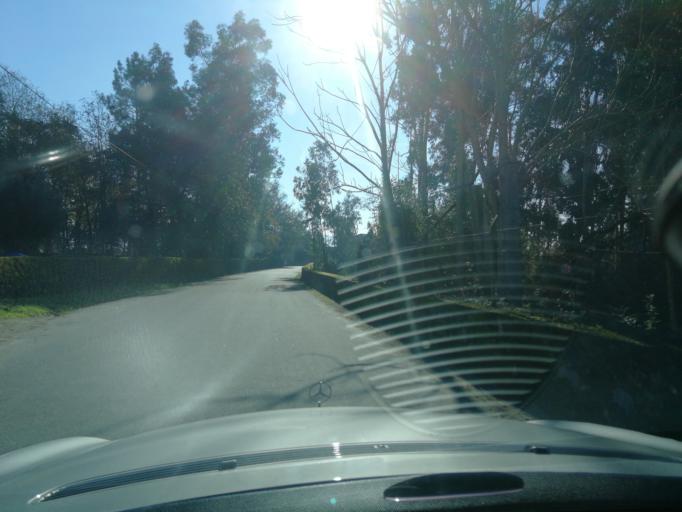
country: PT
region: Braga
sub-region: Braga
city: Adaufe
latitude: 41.6151
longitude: -8.3977
